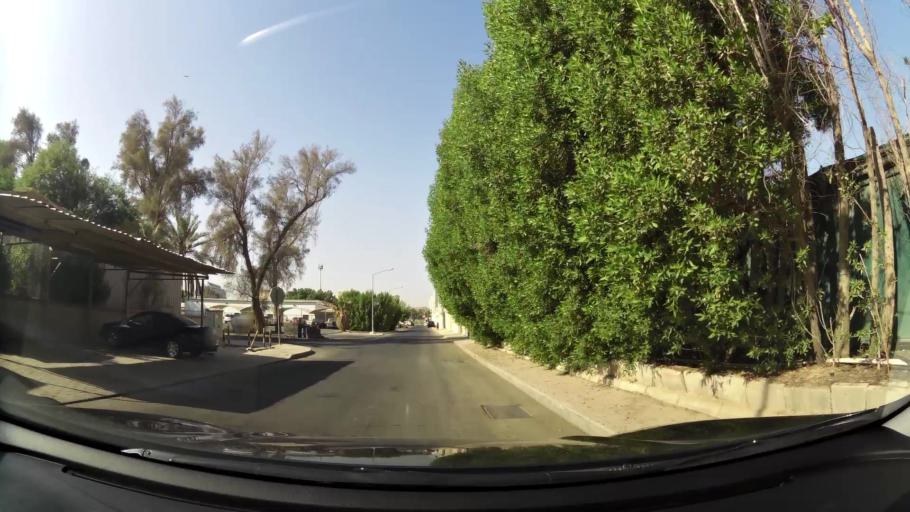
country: KW
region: Al Asimah
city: Ash Shamiyah
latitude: 29.3542
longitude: 47.9467
